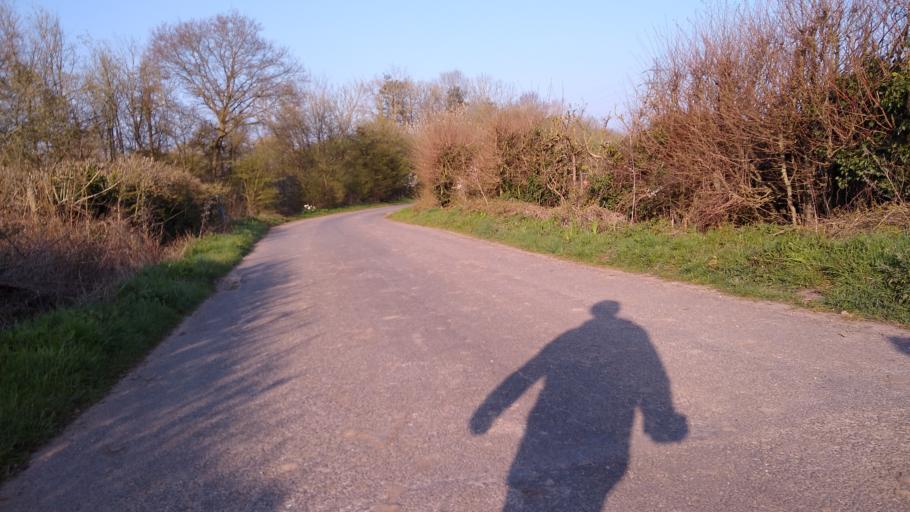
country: GB
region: England
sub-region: Wokingham
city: Winnersh
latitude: 51.4369
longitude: -0.8675
